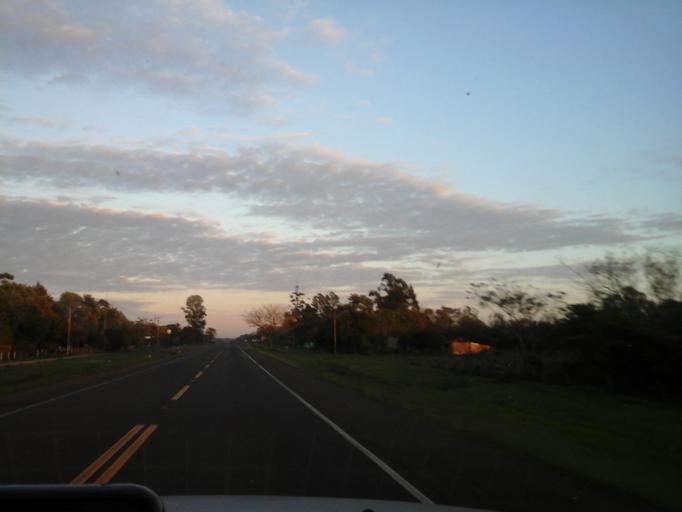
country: PY
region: Itapua
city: General Delgado
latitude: -27.0756
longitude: -56.5803
